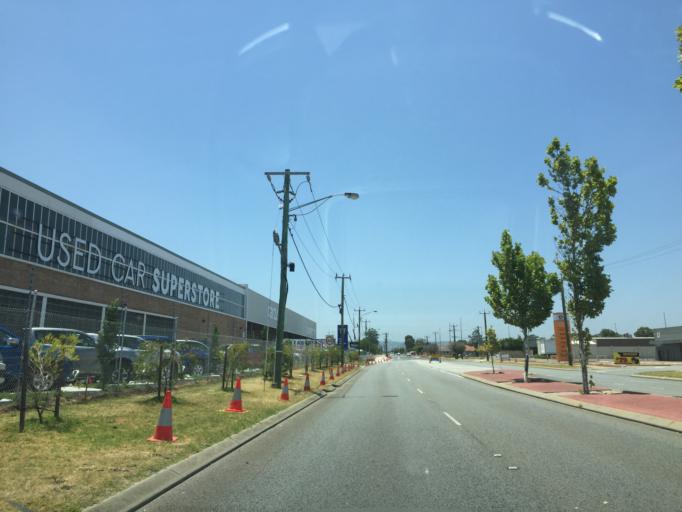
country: AU
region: Western Australia
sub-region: Canning
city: Queens Park
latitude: -31.9955
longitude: 115.9373
